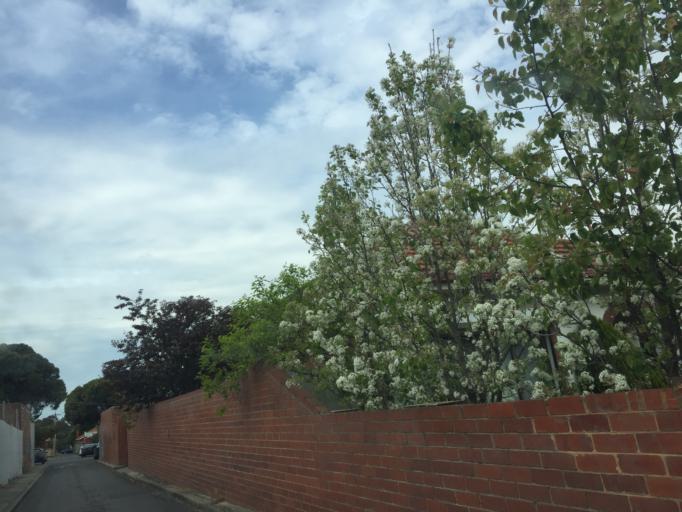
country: AU
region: Victoria
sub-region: Darebin
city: Preston
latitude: -37.7564
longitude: 145.0137
